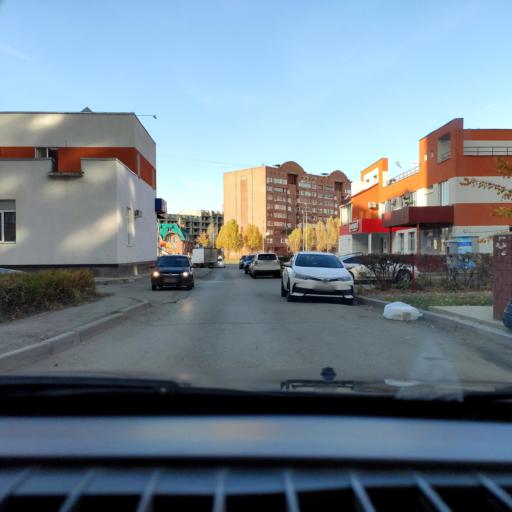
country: RU
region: Samara
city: Tol'yatti
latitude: 53.5359
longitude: 49.3548
